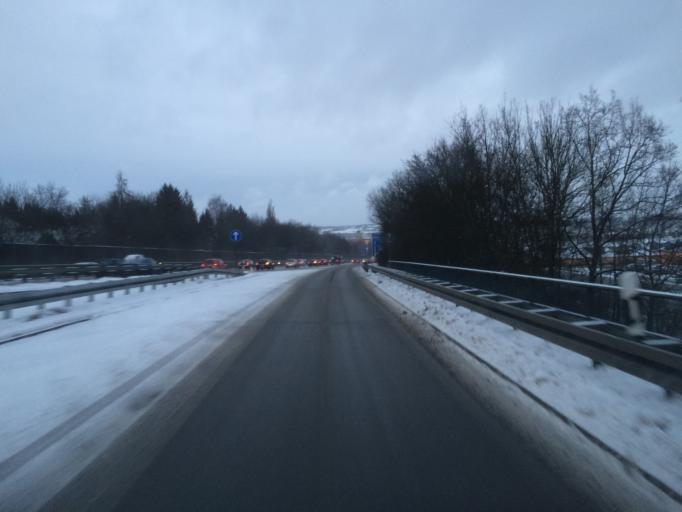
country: DE
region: Bavaria
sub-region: Upper Palatinate
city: Pentling
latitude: 49.0032
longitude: 12.0626
